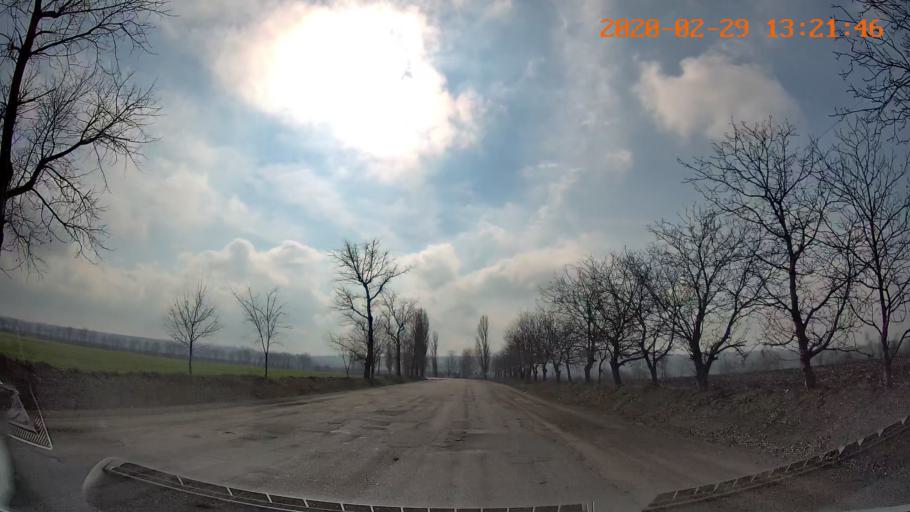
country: MD
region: Telenesti
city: Camenca
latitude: 47.9673
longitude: 28.6301
